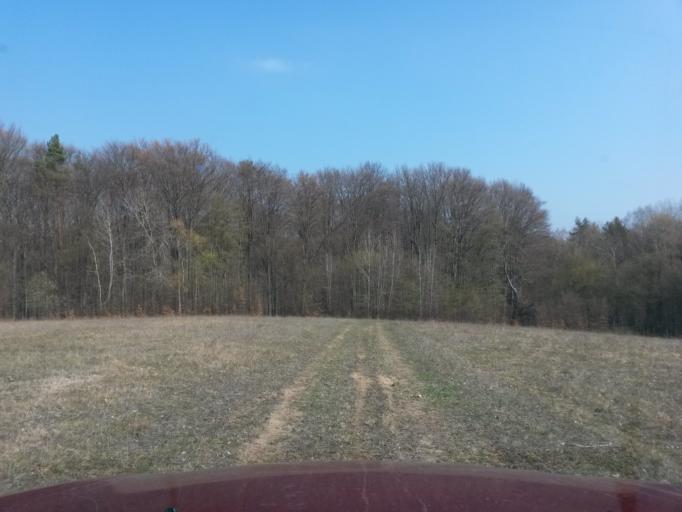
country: SK
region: Presovsky
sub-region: Okres Presov
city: Presov
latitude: 48.9343
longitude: 21.1453
